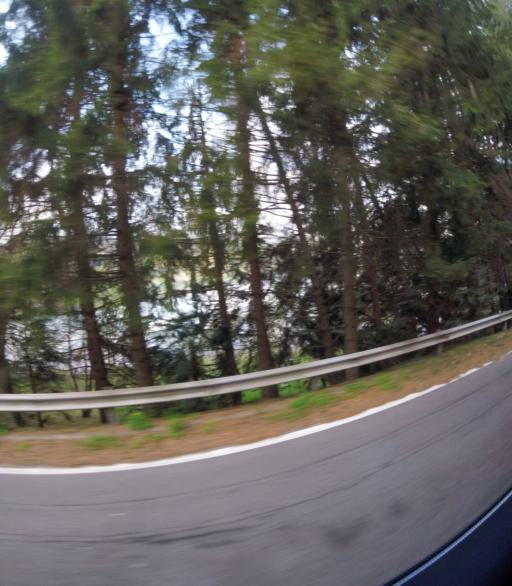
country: IT
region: Piedmont
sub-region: Provincia di Novara
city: Bolzano Novarese
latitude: 45.7668
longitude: 8.4293
